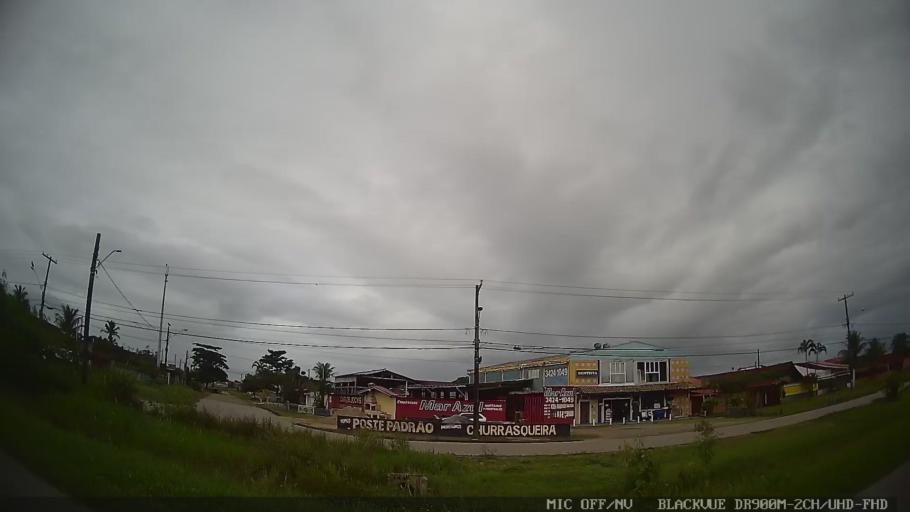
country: BR
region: Sao Paulo
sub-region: Itanhaem
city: Itanhaem
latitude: -24.1481
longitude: -46.7297
